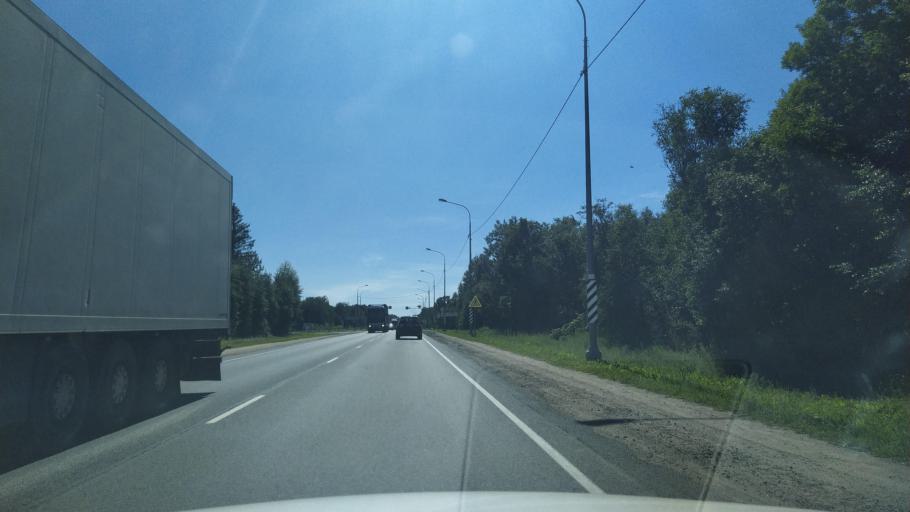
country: RU
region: Pskov
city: Pskov
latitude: 57.7876
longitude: 28.4102
